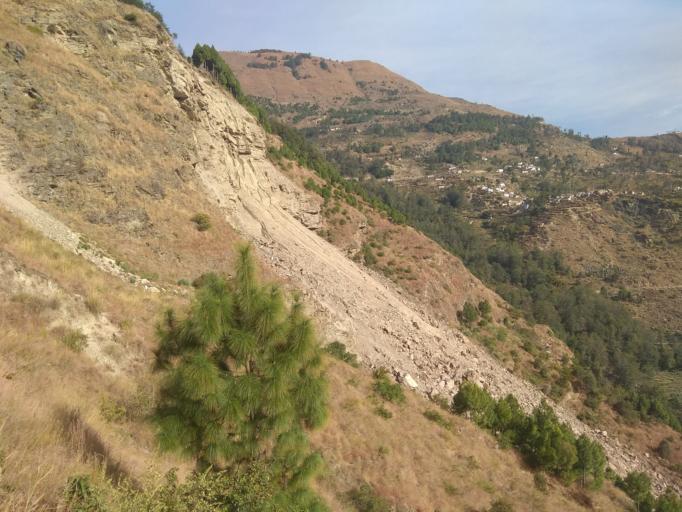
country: NP
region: Mid Western
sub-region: Bheri Zone
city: Dailekh
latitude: 29.2372
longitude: 81.6511
